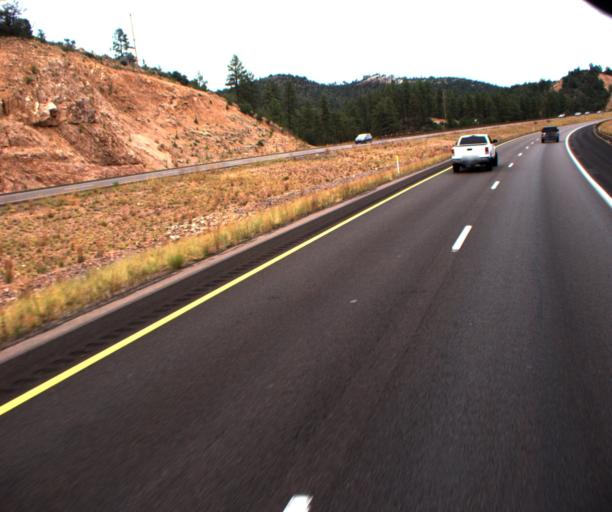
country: US
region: Arizona
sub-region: Gila County
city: Star Valley
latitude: 34.2916
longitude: -111.1368
